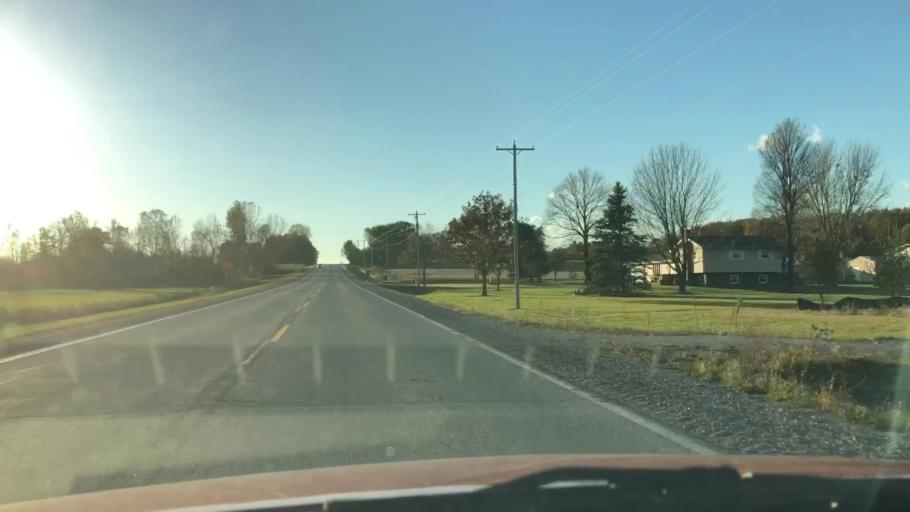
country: US
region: Wisconsin
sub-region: Brown County
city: Oneida
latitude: 44.4443
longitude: -88.2592
